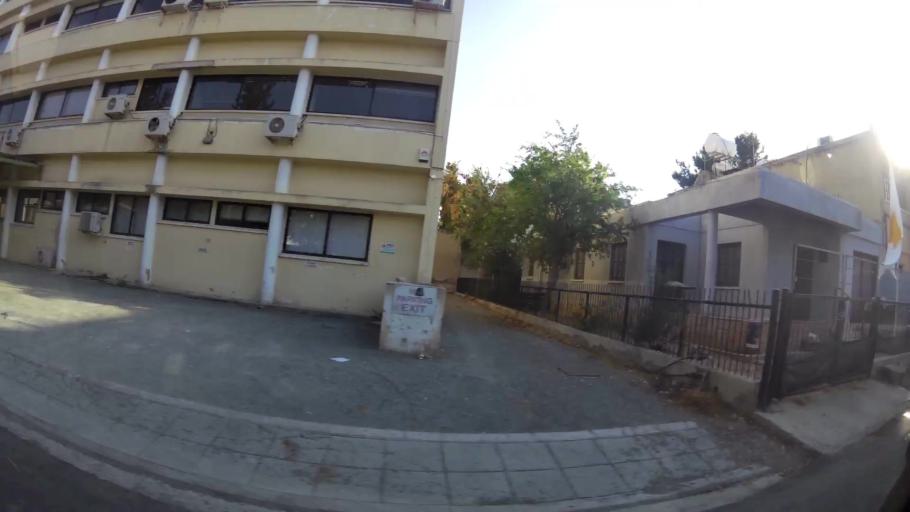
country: CY
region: Lefkosia
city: Nicosia
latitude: 35.1713
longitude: 33.3482
